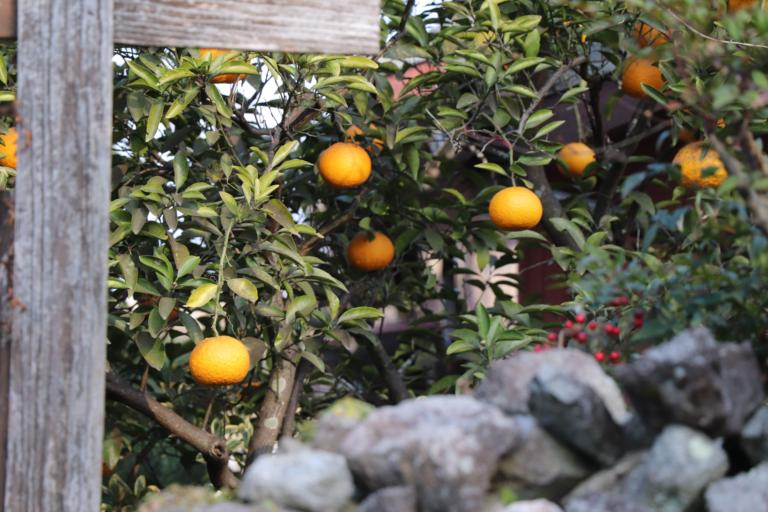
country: JP
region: Nagasaki
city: Shimabara
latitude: 32.7923
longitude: 130.3631
